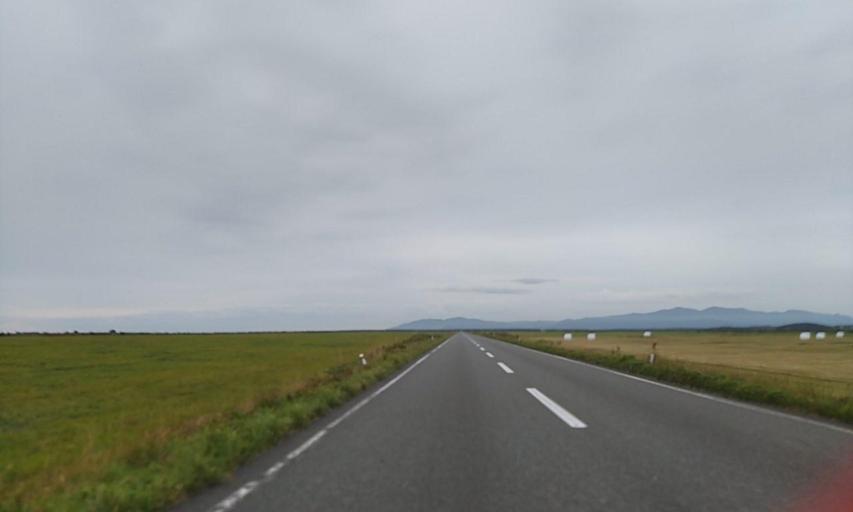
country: JP
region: Hokkaido
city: Makubetsu
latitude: 45.1916
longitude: 142.3105
